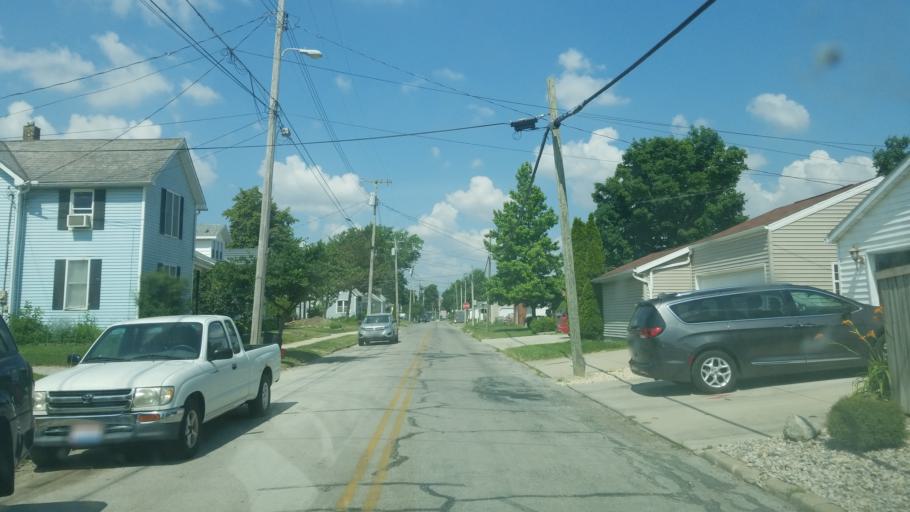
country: US
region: Ohio
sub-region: Auglaize County
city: Wapakoneta
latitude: 40.5699
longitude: -84.1850
